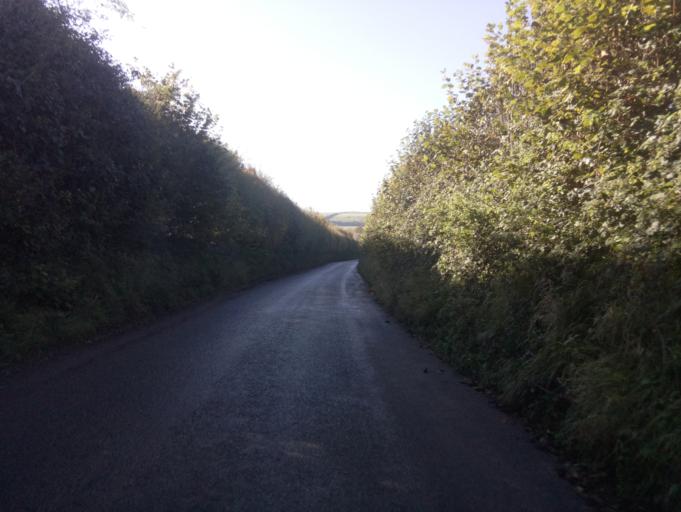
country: GB
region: England
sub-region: Dorset
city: Dorchester
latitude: 50.8123
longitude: -2.4643
